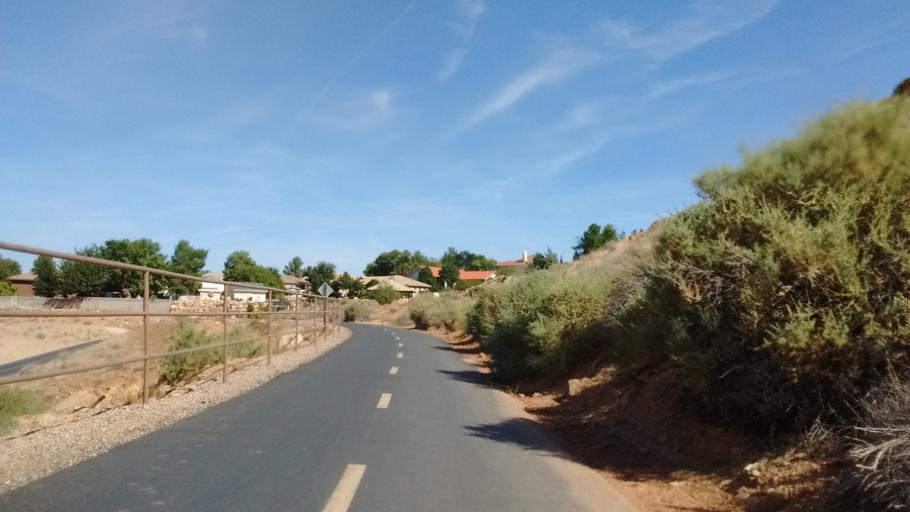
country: US
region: Utah
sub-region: Washington County
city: Saint George
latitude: 37.0716
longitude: -113.5790
